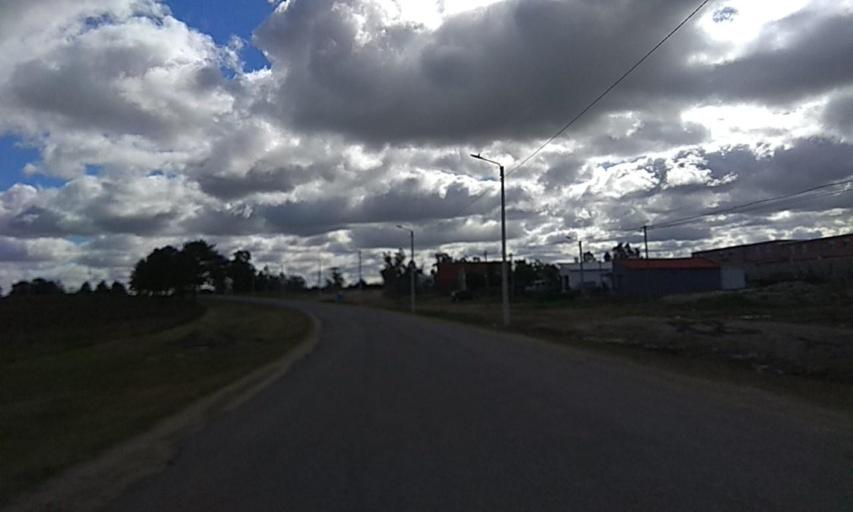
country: UY
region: Florida
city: Florida
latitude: -34.0811
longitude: -56.2260
